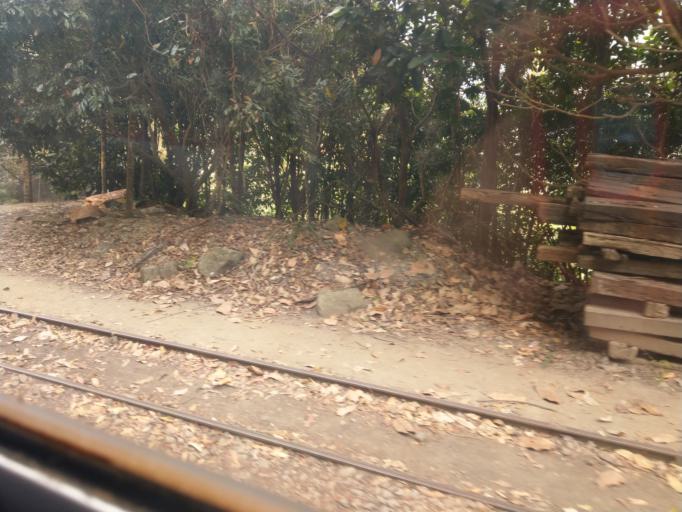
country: TW
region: Taiwan
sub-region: Chiayi
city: Jiayi Shi
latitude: 23.5389
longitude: 120.6072
